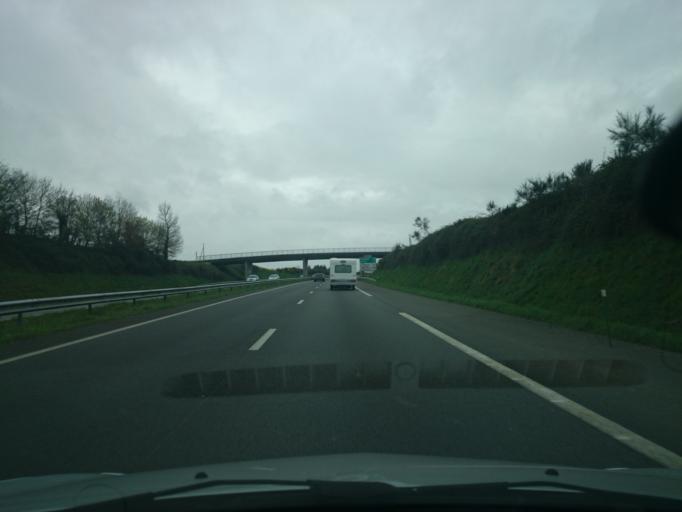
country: FR
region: Brittany
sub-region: Departement des Cotes-d'Armor
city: Plenee-Jugon
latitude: 48.3781
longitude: -2.3661
